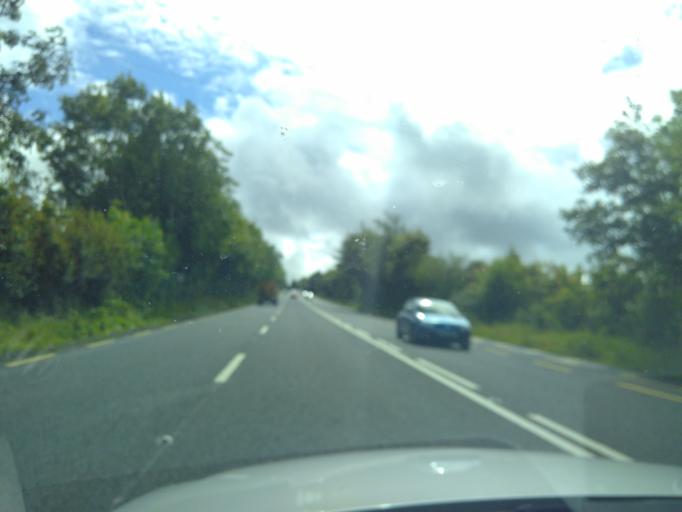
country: IE
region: Ulster
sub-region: County Donegal
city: Letterkenny
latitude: 54.9369
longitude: -7.6961
